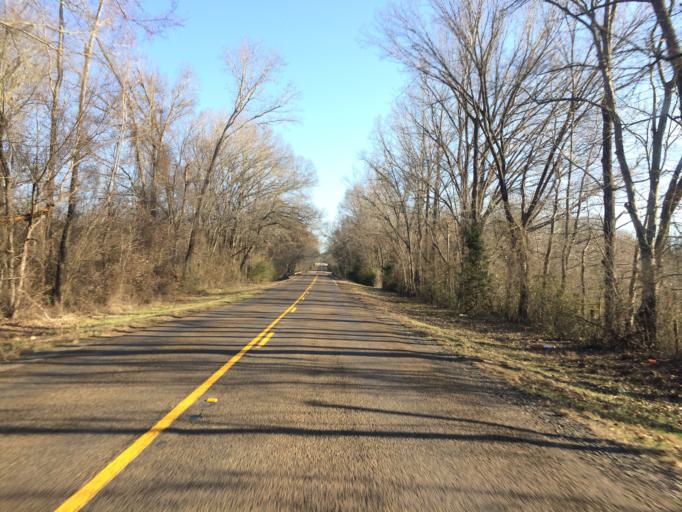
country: US
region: Texas
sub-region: Wood County
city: Quitman
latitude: 32.7117
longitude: -95.3628
